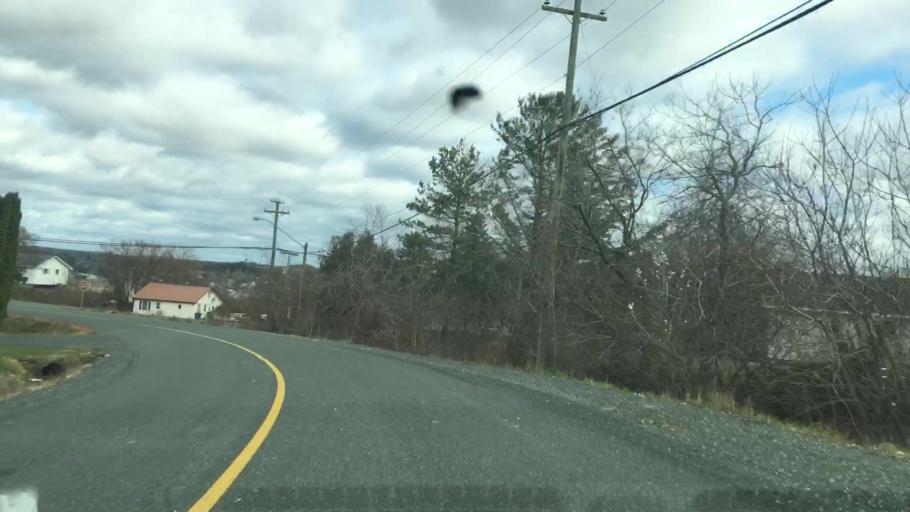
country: CA
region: New Brunswick
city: Florenceville-Bristol
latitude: 46.2904
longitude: -67.5336
